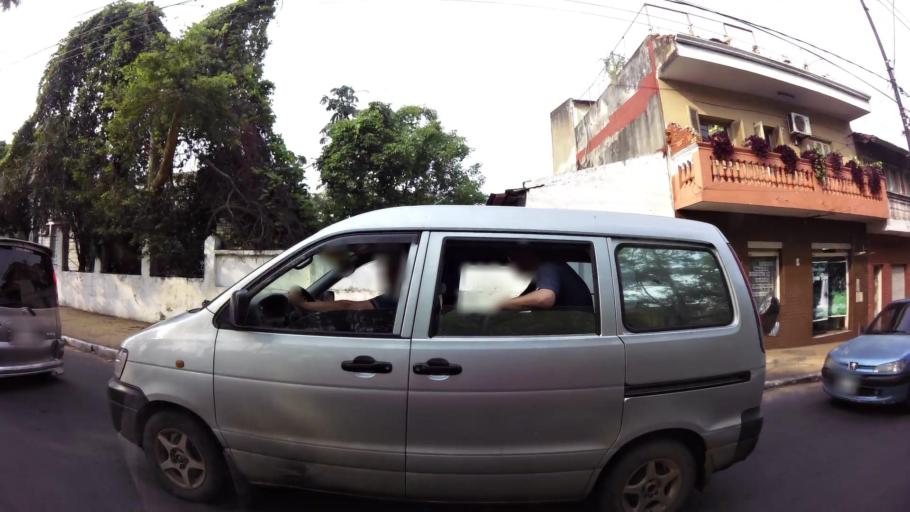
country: PY
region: Asuncion
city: Asuncion
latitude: -25.2953
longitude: -57.6313
